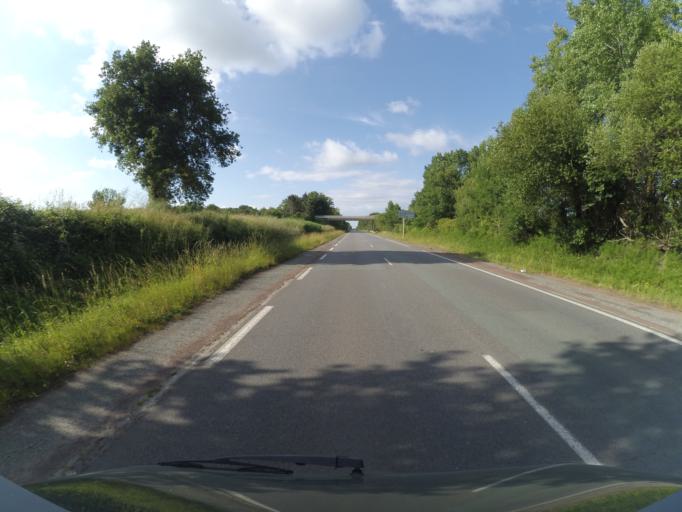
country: FR
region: Poitou-Charentes
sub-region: Departement de la Charente-Maritime
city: Le Gua
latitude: 45.7827
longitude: -0.9362
